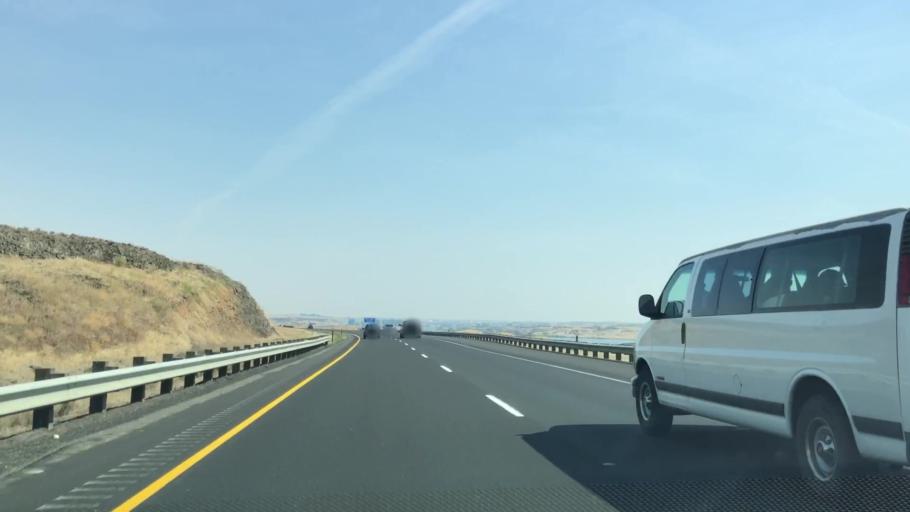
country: US
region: Washington
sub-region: Adams County
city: Ritzville
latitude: 47.2670
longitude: -118.0644
